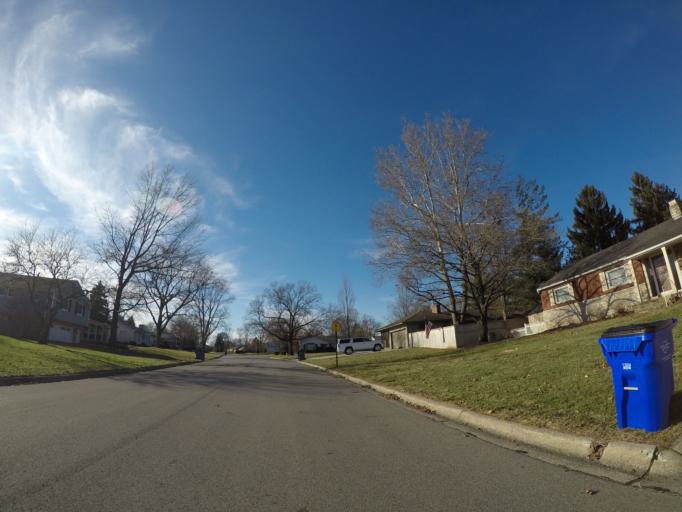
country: US
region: Ohio
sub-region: Franklin County
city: Upper Arlington
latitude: 40.0202
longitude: -83.0530
